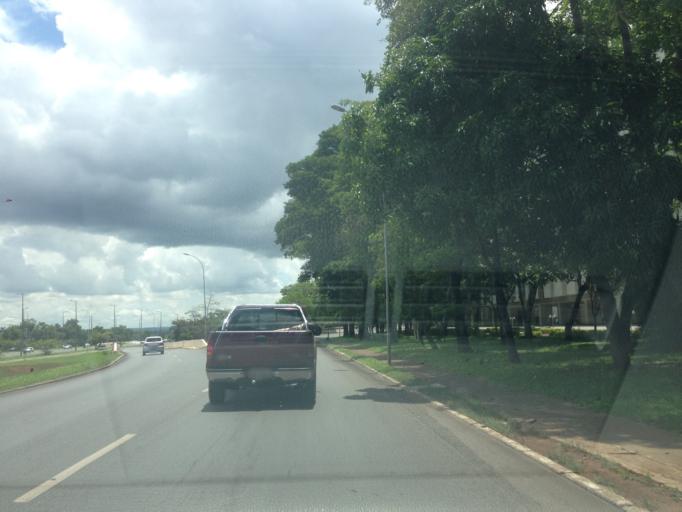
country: BR
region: Federal District
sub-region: Brasilia
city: Brasilia
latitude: -15.8332
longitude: -47.9245
